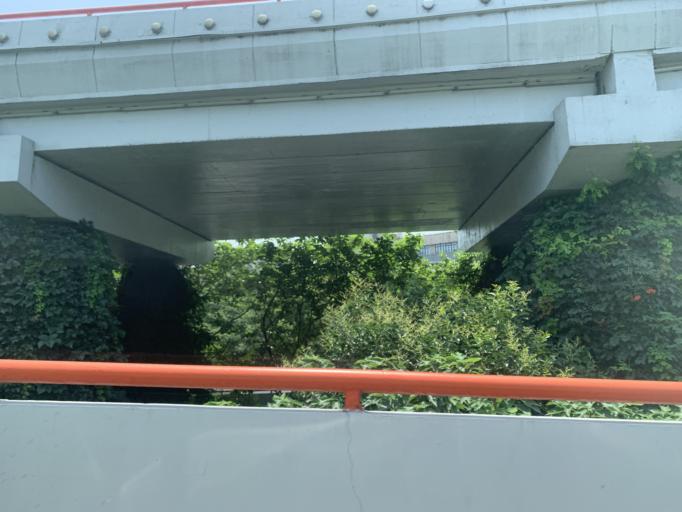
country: CN
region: Shanghai Shi
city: Huamu
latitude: 31.2003
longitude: 121.5242
